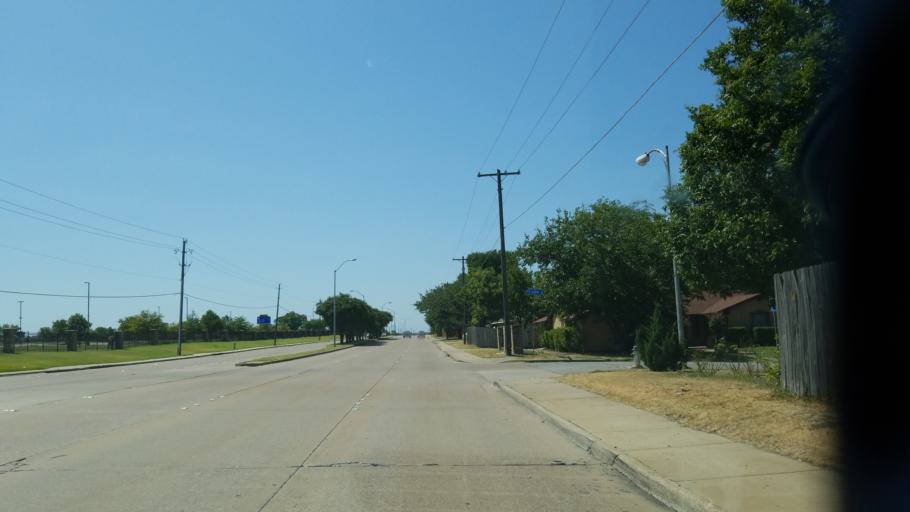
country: US
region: Texas
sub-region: Dallas County
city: Duncanville
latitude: 32.6526
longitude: -96.8914
